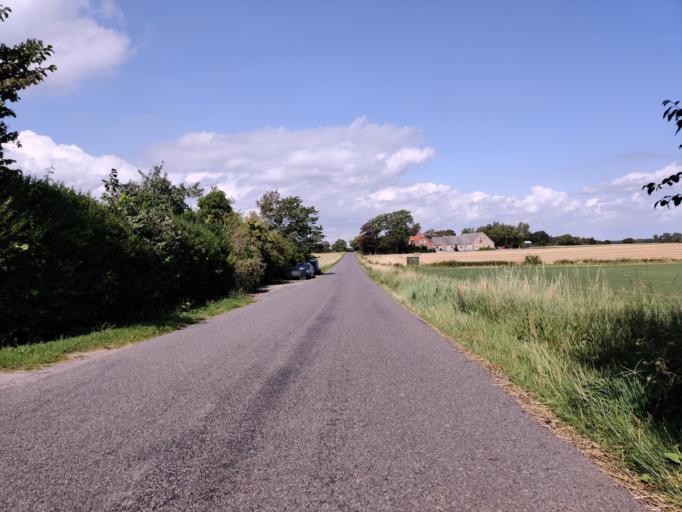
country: DK
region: Zealand
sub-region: Guldborgsund Kommune
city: Nykobing Falster
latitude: 54.6603
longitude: 11.8895
